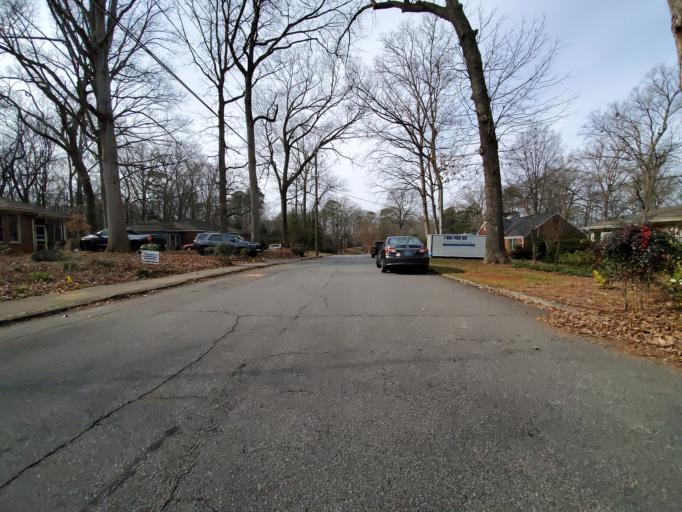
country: US
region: Georgia
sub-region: DeKalb County
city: Druid Hills
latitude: 33.7797
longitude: -84.3192
